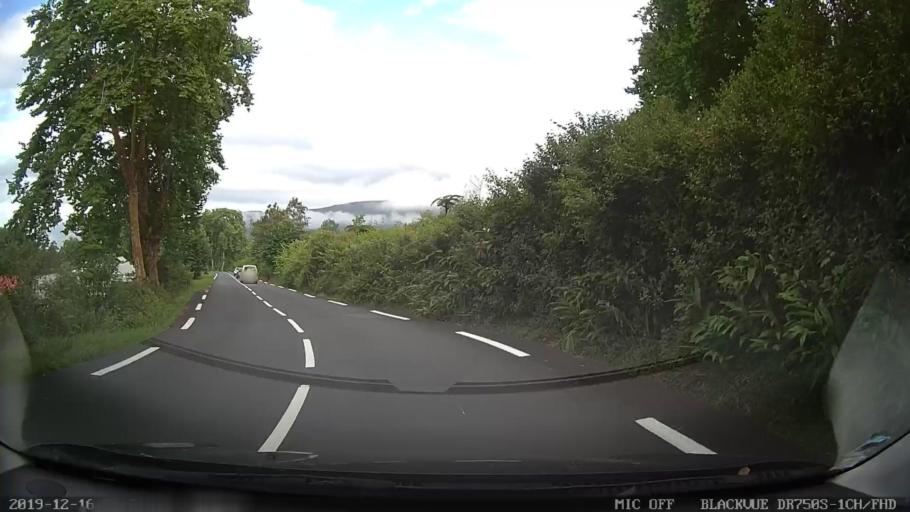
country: RE
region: Reunion
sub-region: Reunion
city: Cilaos
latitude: -21.1508
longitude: 55.6145
